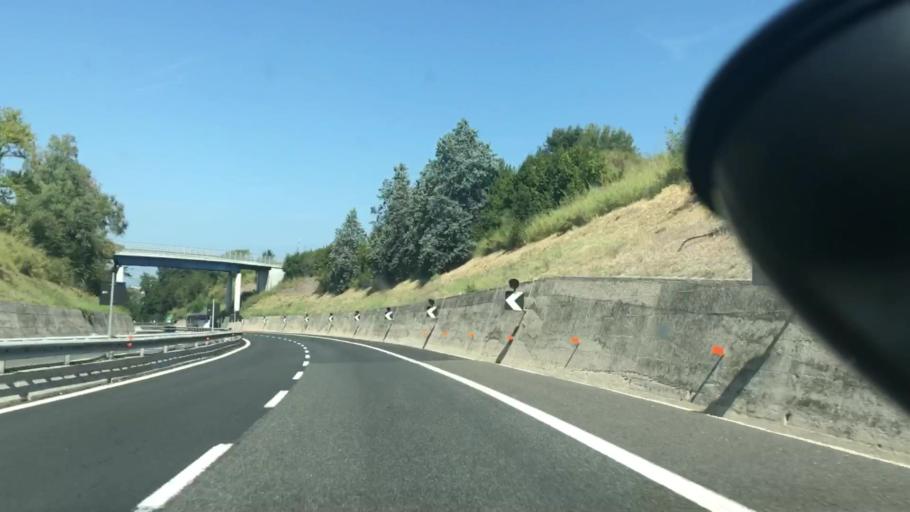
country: IT
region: Abruzzo
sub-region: Provincia di Chieti
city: Marina di San Vito
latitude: 42.3089
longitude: 14.4220
